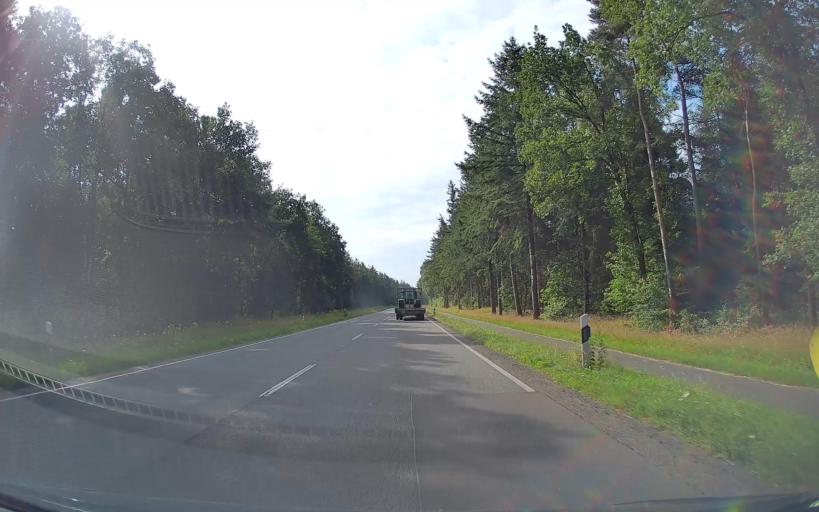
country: DE
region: Lower Saxony
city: Bosel
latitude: 52.9702
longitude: 7.9152
